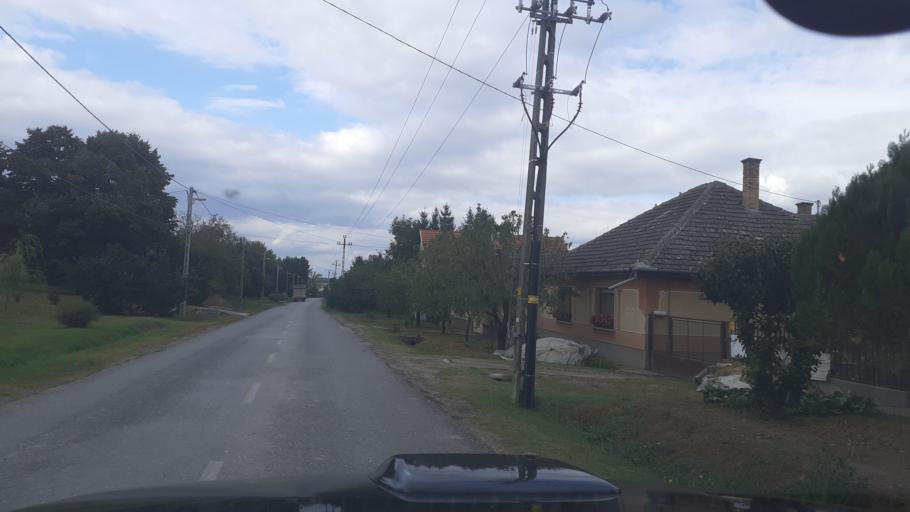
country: HU
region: Tolna
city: Dunafoldvar
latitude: 46.8362
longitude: 18.9532
